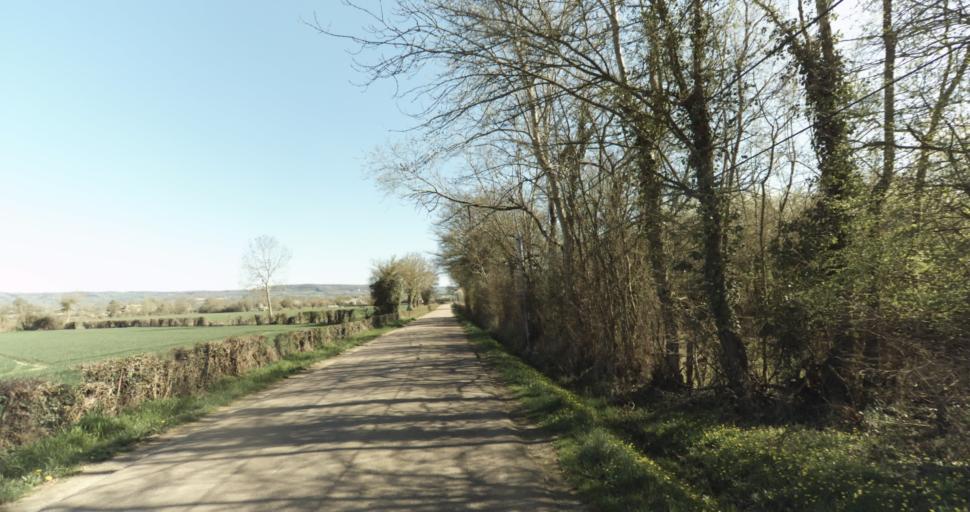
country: FR
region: Lower Normandy
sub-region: Departement du Calvados
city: Saint-Pierre-sur-Dives
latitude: 48.9597
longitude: 0.0044
